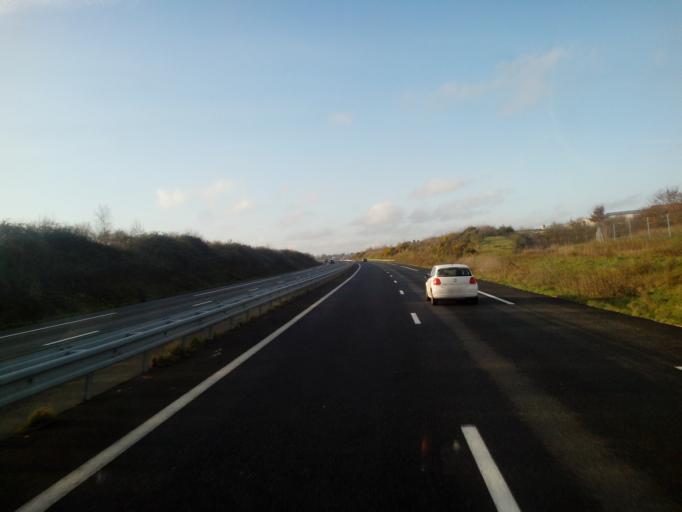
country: FR
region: Poitou-Charentes
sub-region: Departement des Deux-Sevres
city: Saint-Pierre-des-Echaubrognes
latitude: 46.9619
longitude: -0.7871
